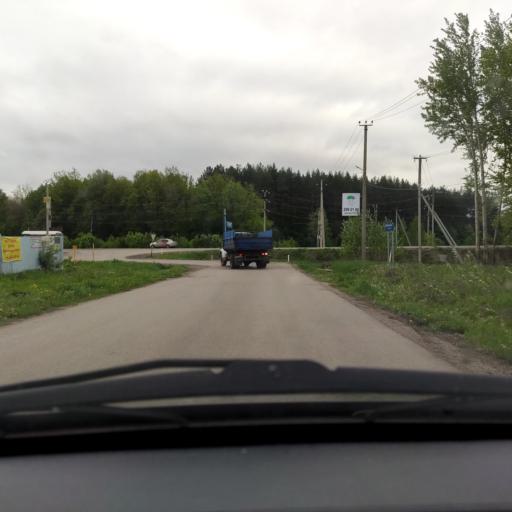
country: RU
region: Bashkortostan
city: Kabakovo
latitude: 54.6139
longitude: 56.1591
